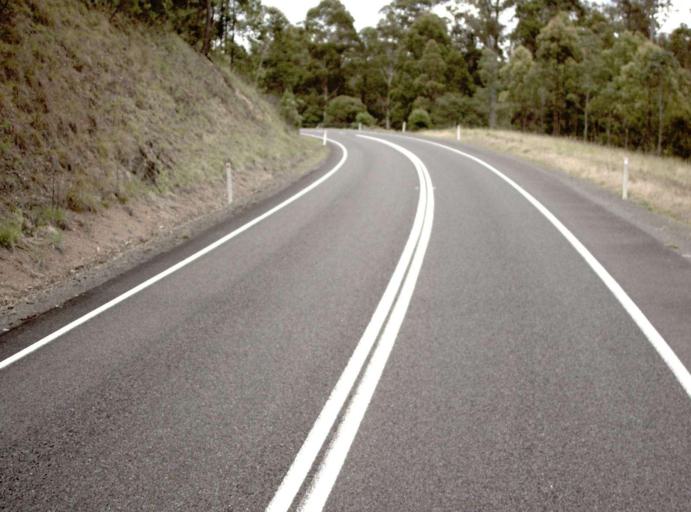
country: AU
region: New South Wales
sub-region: Bombala
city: Bombala
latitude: -37.2578
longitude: 149.2394
